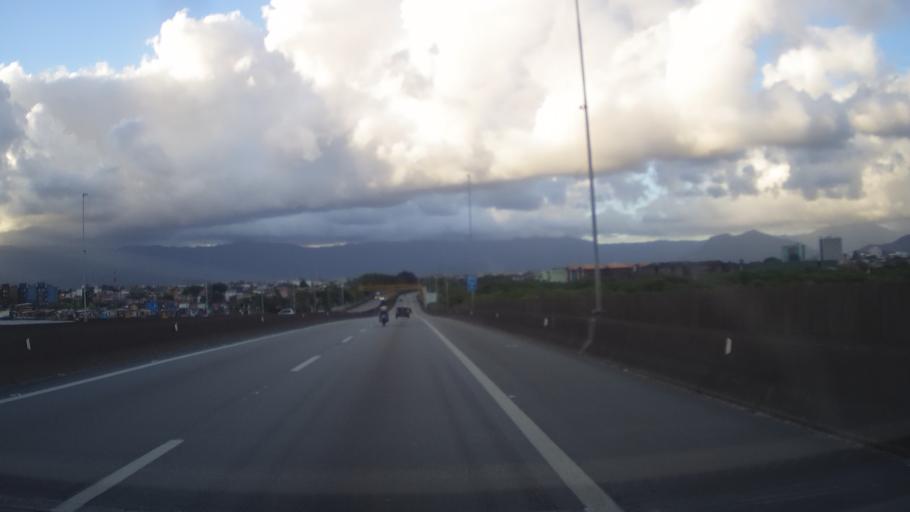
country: BR
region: Sao Paulo
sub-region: Sao Vicente
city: Sao Vicente
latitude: -23.9789
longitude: -46.4013
